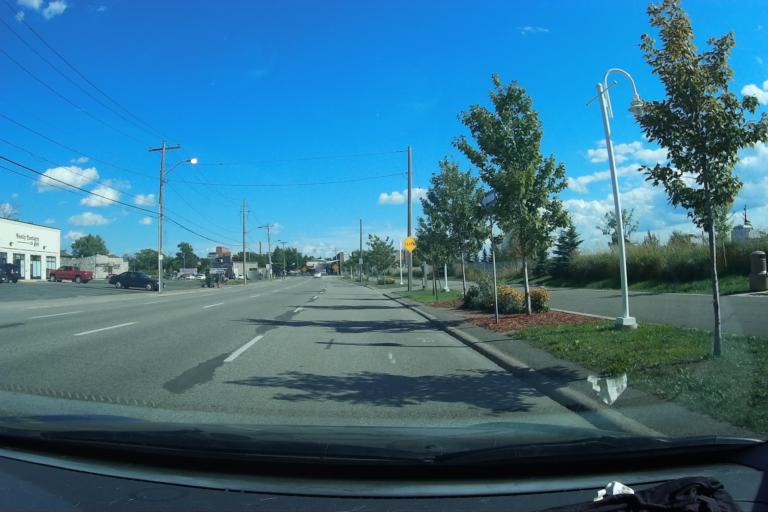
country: CA
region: Ontario
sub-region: Algoma
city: Sault Ste. Marie
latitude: 46.5061
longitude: -84.3273
